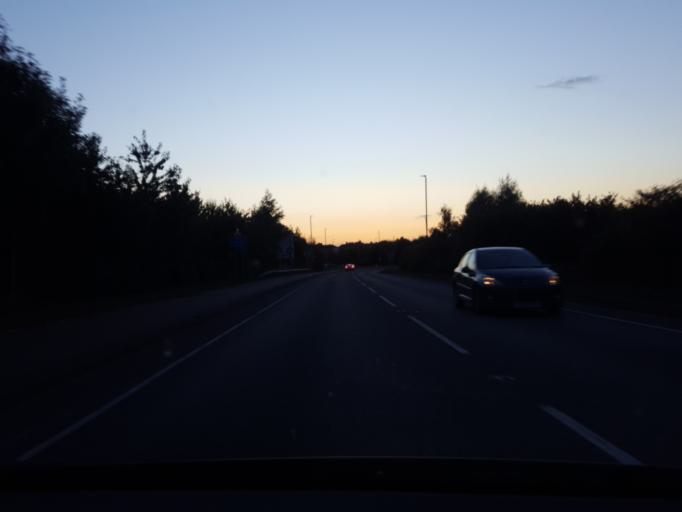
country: GB
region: England
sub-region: Leicestershire
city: Loughborough
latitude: 52.7537
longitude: -1.1937
